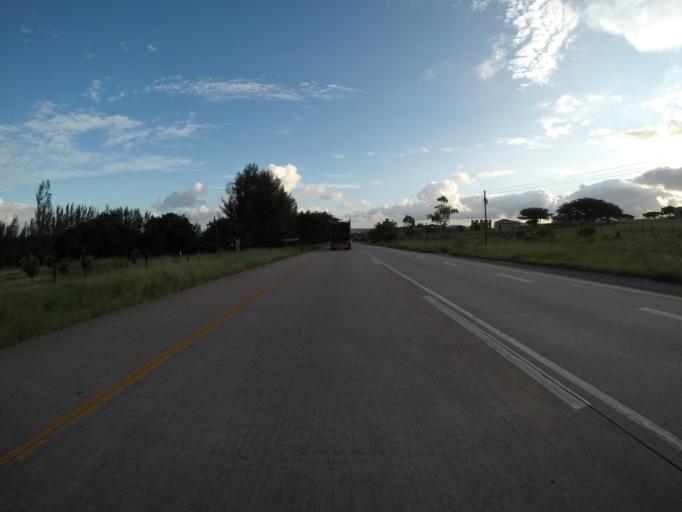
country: ZA
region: KwaZulu-Natal
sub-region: uMkhanyakude District Municipality
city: Mtubatuba
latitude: -28.4774
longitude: 32.1444
